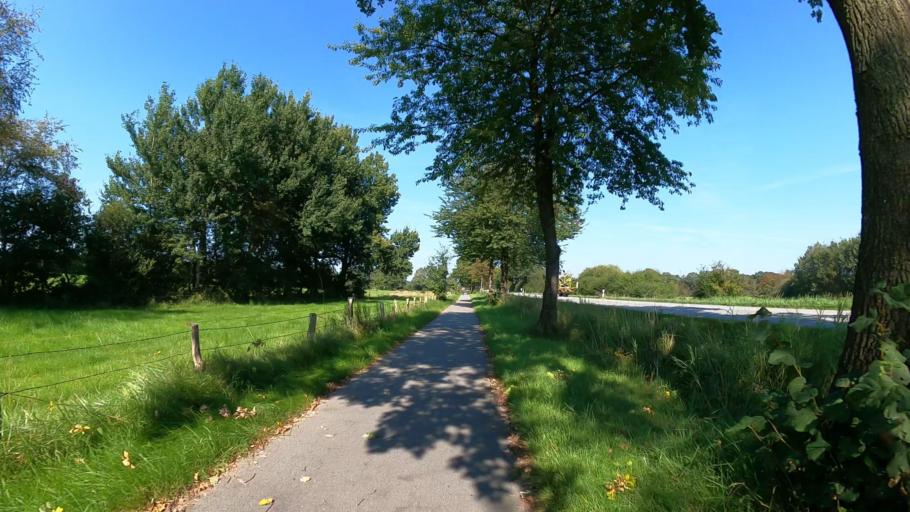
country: DE
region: Schleswig-Holstein
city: Lentfohrden
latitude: 53.8865
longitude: 9.8860
